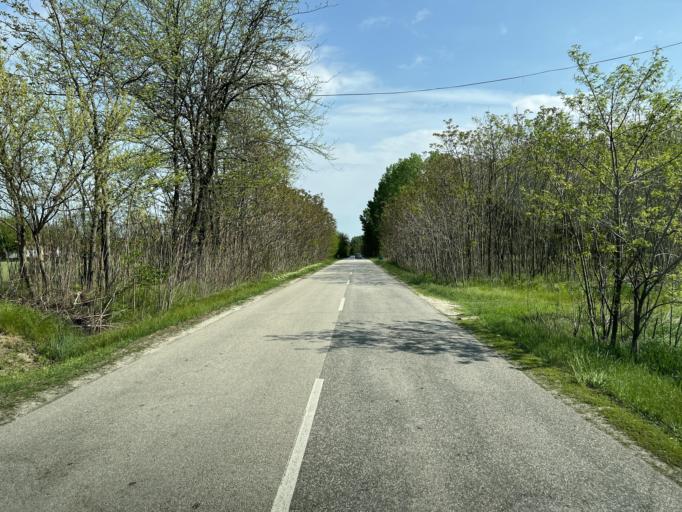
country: HU
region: Pest
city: Kocser
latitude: 47.0179
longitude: 19.9319
